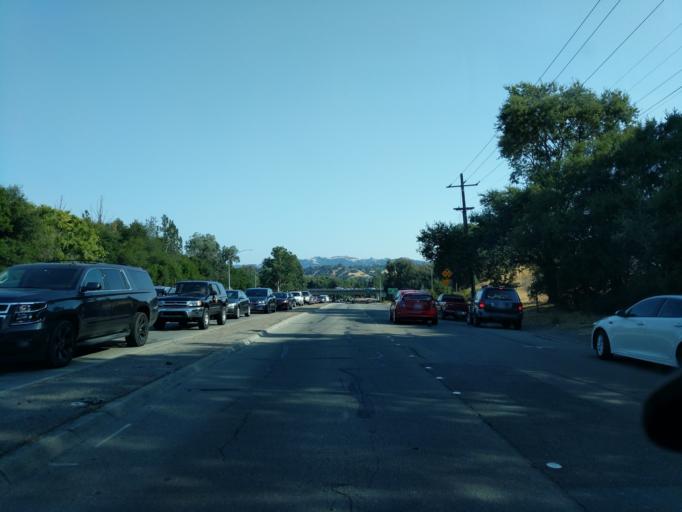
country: US
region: California
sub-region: Contra Costa County
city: Lafayette
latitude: 37.9007
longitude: -122.0972
